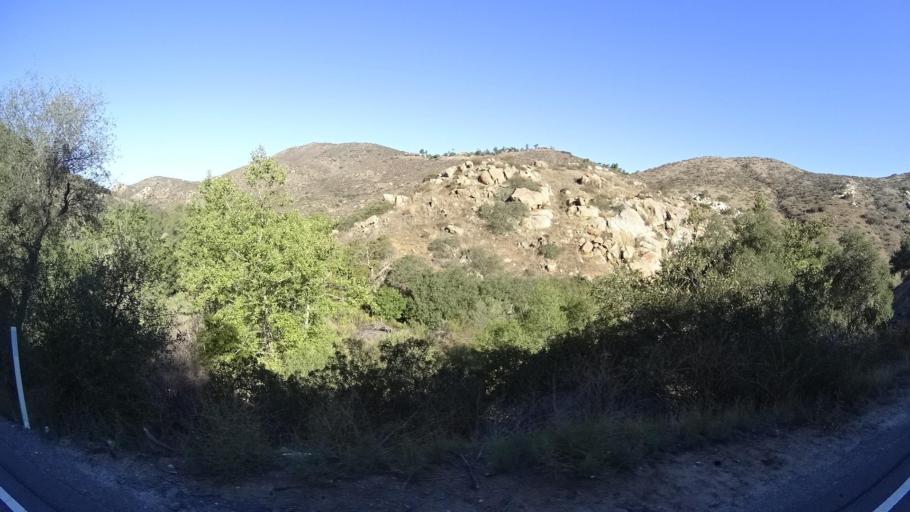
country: US
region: California
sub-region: San Diego County
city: Jamul
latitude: 32.6528
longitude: -116.7906
